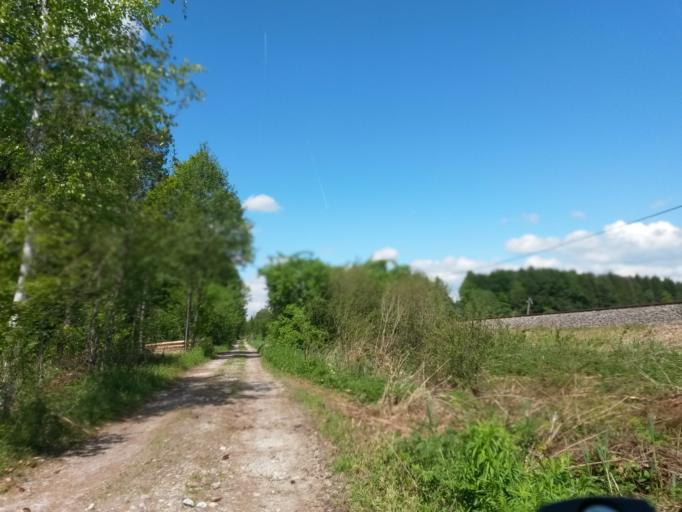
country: DE
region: Baden-Wuerttemberg
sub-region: Tuebingen Region
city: Bad Waldsee
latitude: 47.9399
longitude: 9.7145
